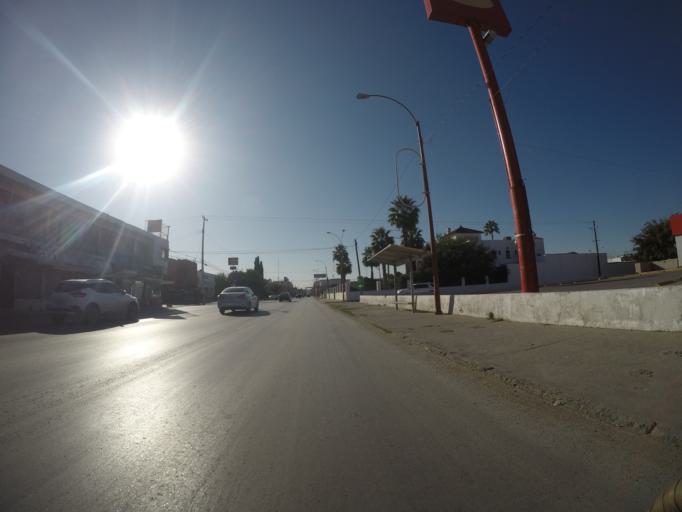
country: MX
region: Chihuahua
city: Ciudad Juarez
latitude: 31.7384
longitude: -106.4701
